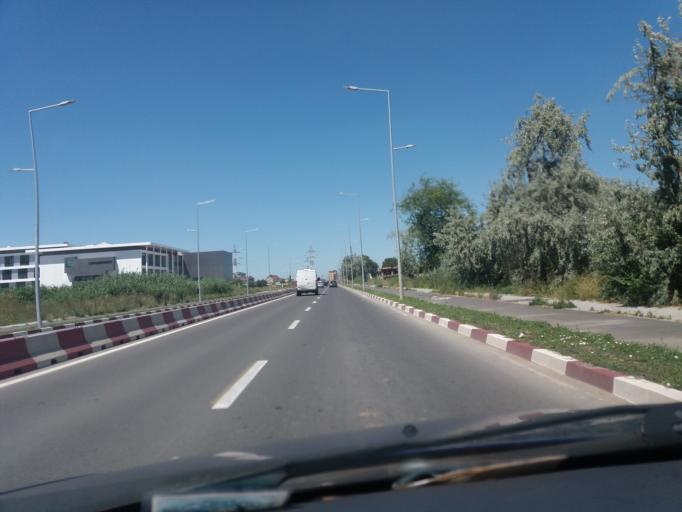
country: RO
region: Constanta
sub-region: Comuna Navodari
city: Navodari
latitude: 44.3155
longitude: 28.6268
